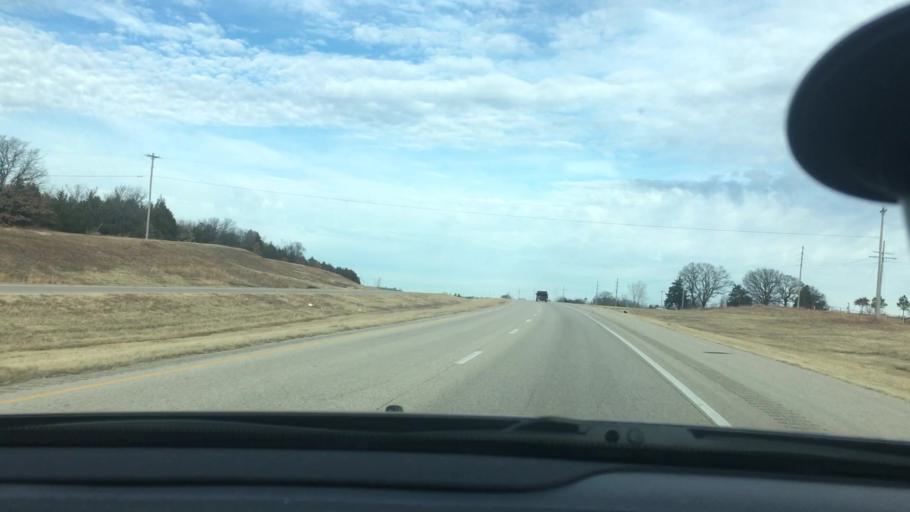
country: US
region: Oklahoma
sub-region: Pontotoc County
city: Byng
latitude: 34.9003
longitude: -96.6749
